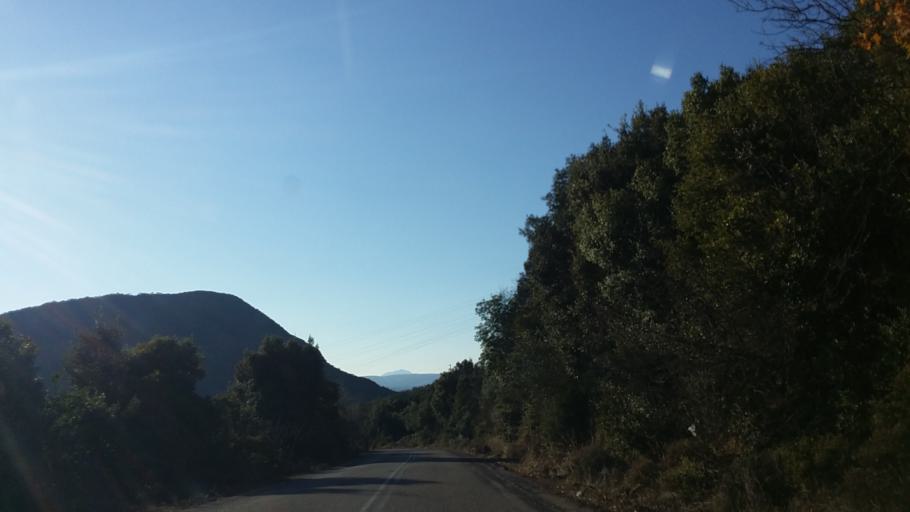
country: GR
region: West Greece
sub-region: Nomos Aitolias kai Akarnanias
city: Neapolis
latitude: 38.7968
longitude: 21.4599
